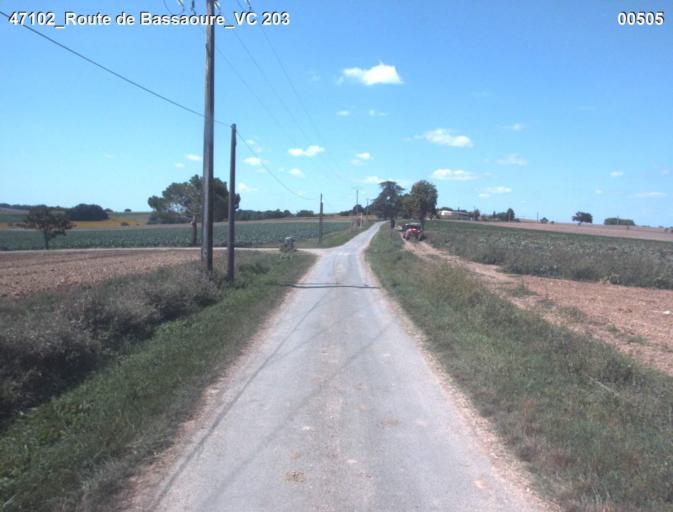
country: FR
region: Aquitaine
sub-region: Departement du Lot-et-Garonne
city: Nerac
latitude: 44.0565
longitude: 0.4284
